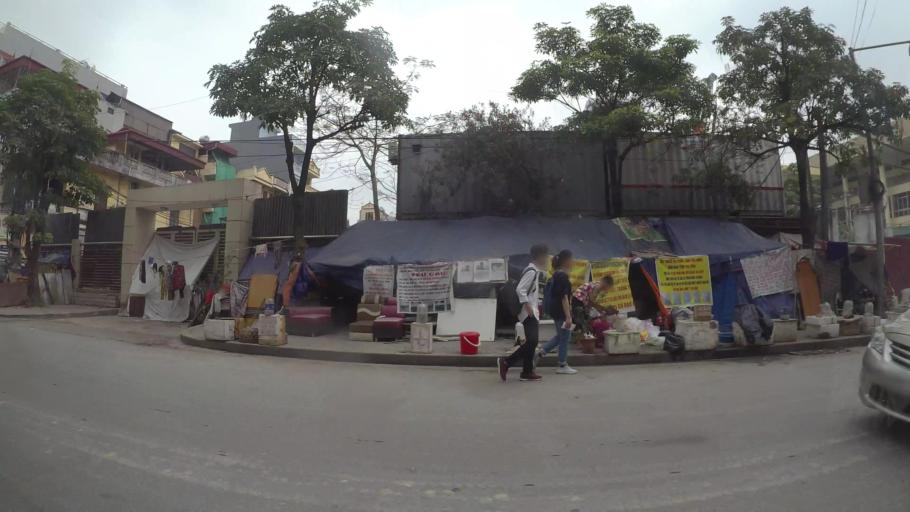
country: VN
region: Ha Noi
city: Ha Dong
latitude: 20.9681
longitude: 105.7697
